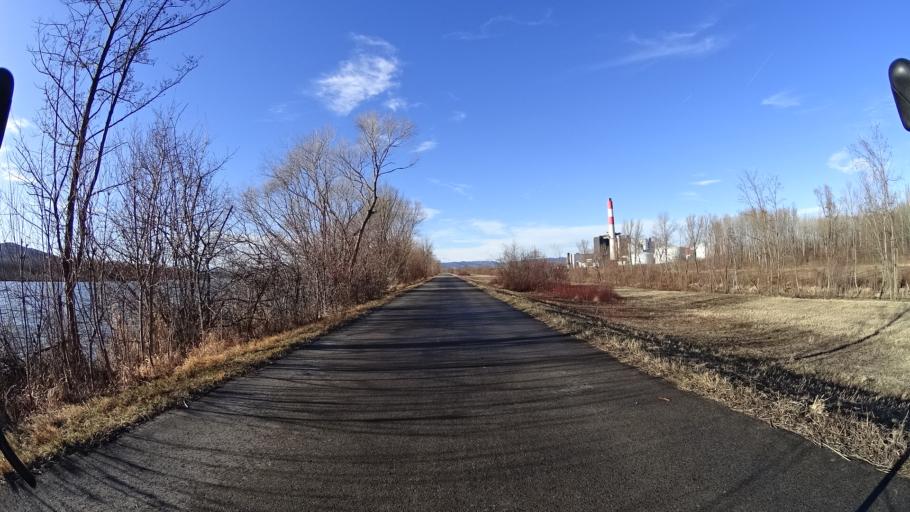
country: AT
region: Lower Austria
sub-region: Politischer Bezirk Krems
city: Grafenegg
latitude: 48.3884
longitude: 15.7168
